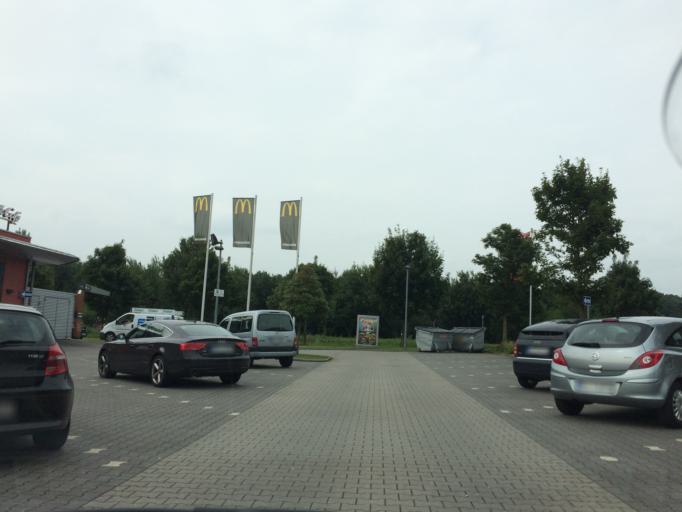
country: DE
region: North Rhine-Westphalia
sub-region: Regierungsbezirk Munster
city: Heiden
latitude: 51.7546
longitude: 6.9637
